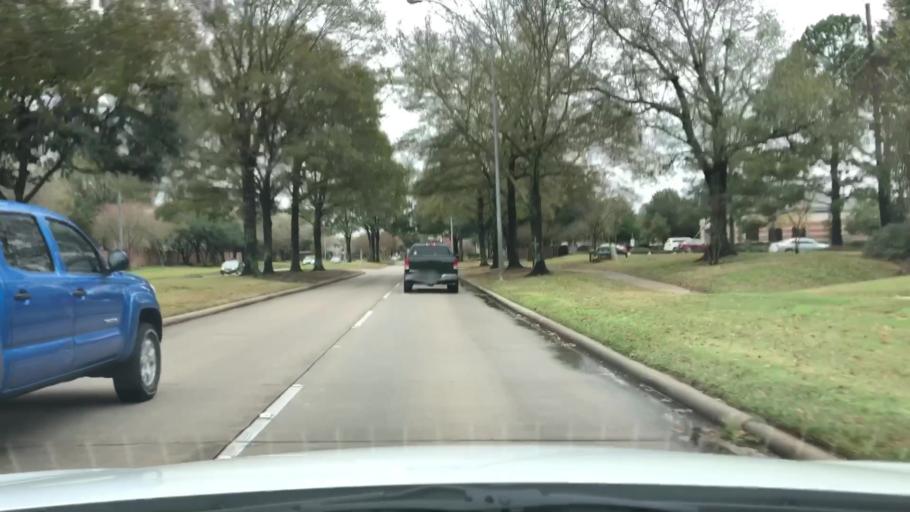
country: US
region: Texas
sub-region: Fort Bend County
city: Cinco Ranch
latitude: 29.7427
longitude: -95.7513
